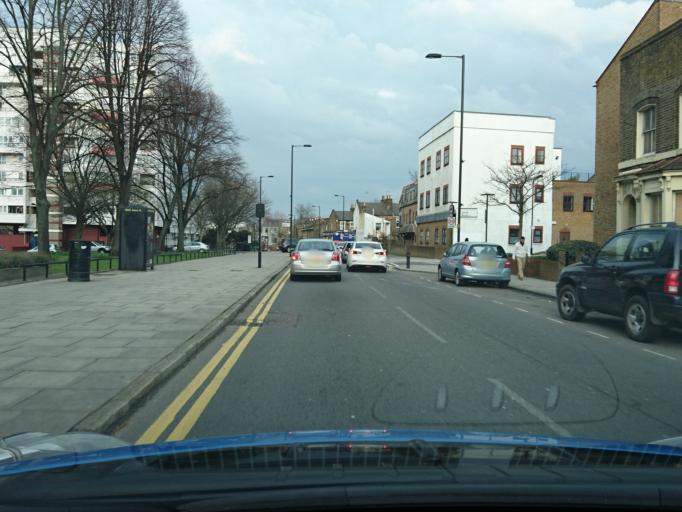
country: GB
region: England
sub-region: Greater London
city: Hackney
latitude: 51.5441
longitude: -0.0385
